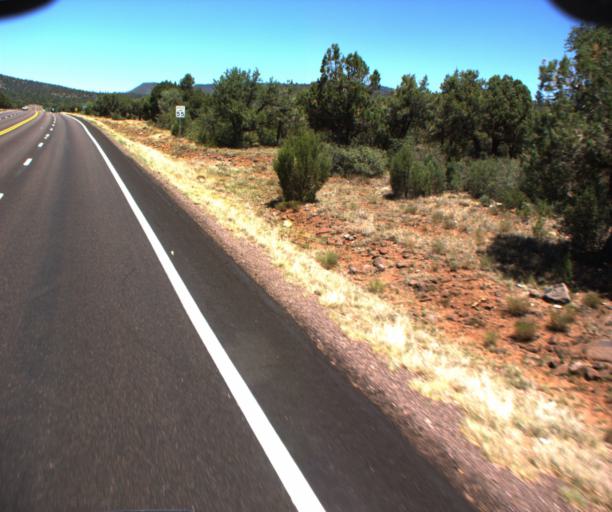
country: US
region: Arizona
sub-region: Gila County
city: Pine
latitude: 34.3288
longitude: -111.4184
